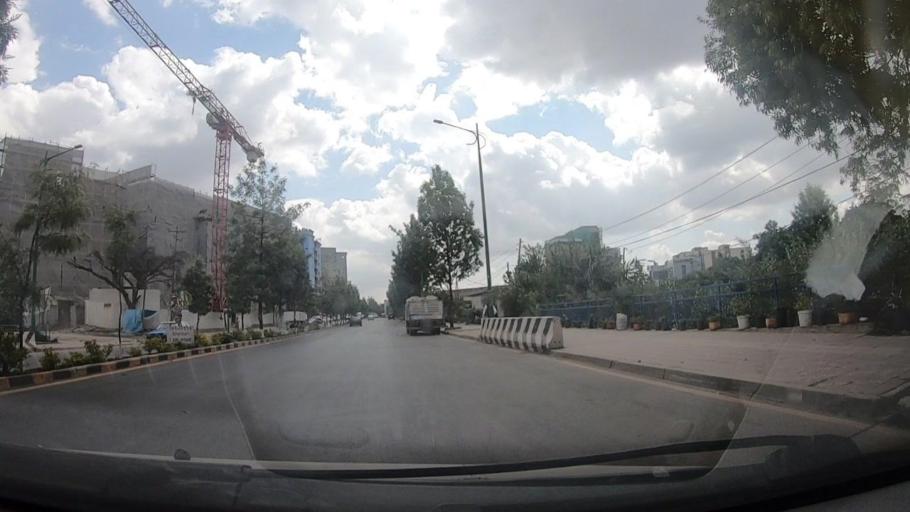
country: ET
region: Adis Abeba
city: Addis Ababa
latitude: 9.0020
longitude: 38.7366
